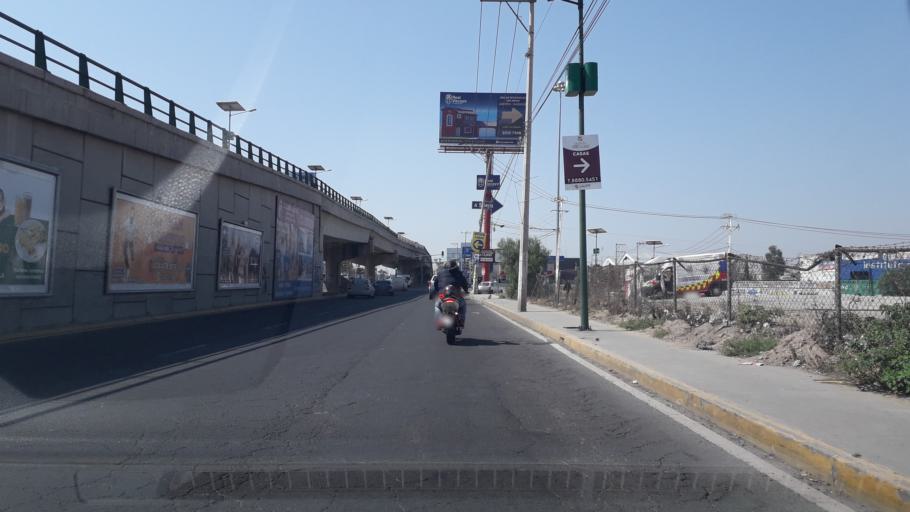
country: MX
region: Mexico
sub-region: Tecamac
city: Ojo de Agua
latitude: 19.6609
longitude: -99.0046
